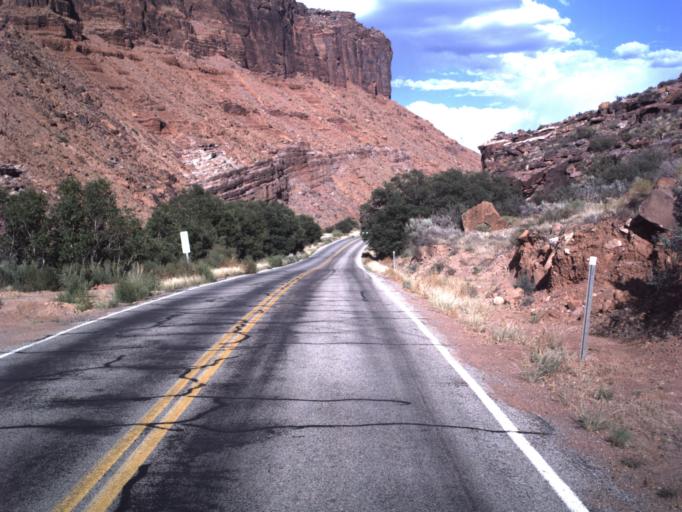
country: US
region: Utah
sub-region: Grand County
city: Moab
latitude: 38.6838
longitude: -109.4689
